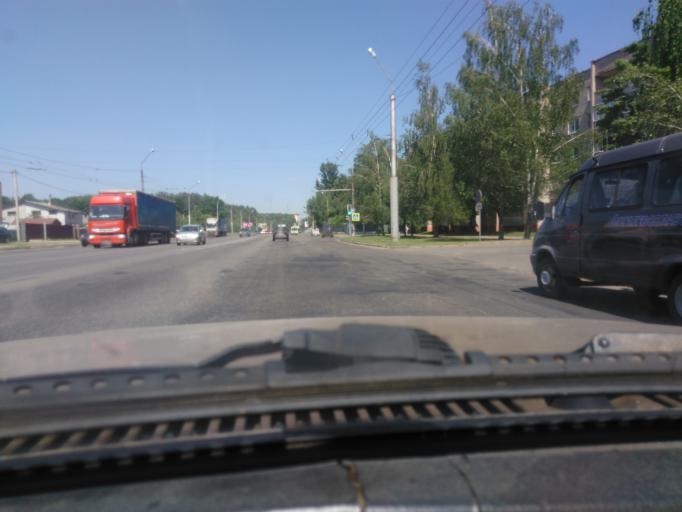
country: BY
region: Mogilev
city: Mahilyow
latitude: 53.9416
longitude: 30.3547
